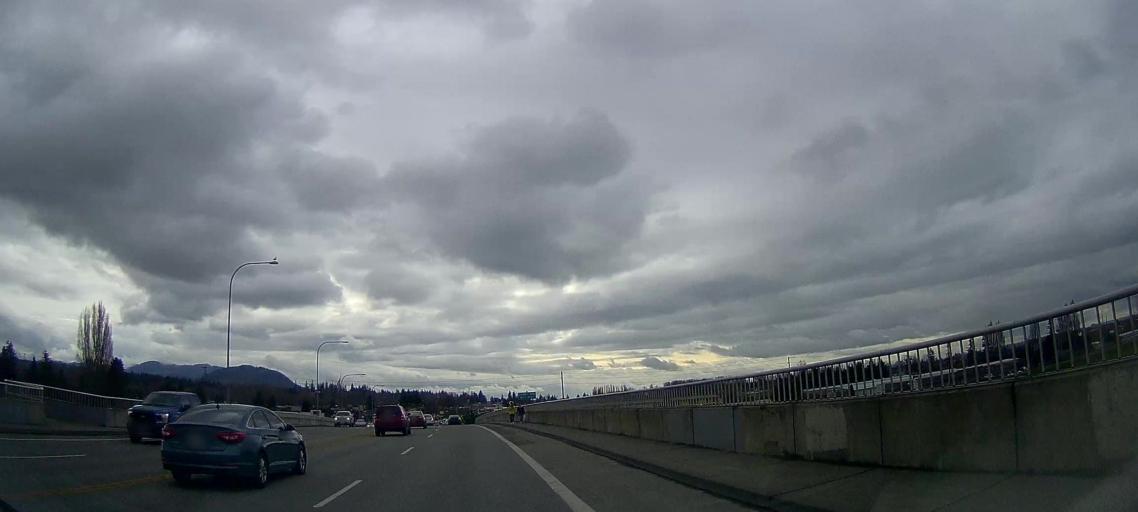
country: US
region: Washington
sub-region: Skagit County
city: Mount Vernon
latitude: 48.4441
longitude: -122.3323
